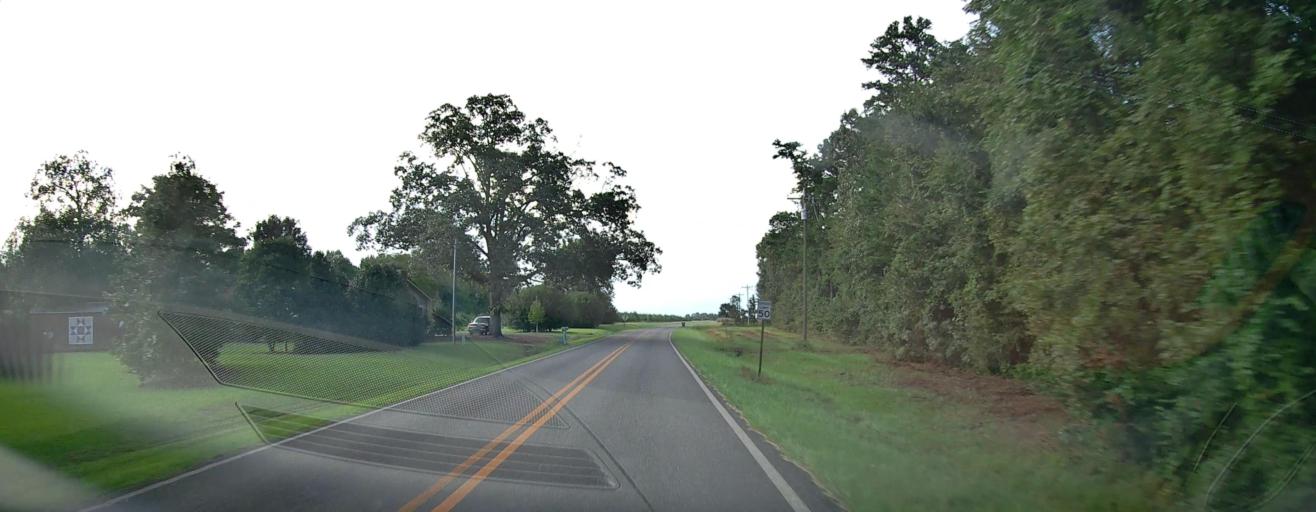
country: US
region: Georgia
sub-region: Pulaski County
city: Hawkinsville
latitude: 32.2962
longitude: -83.5526
